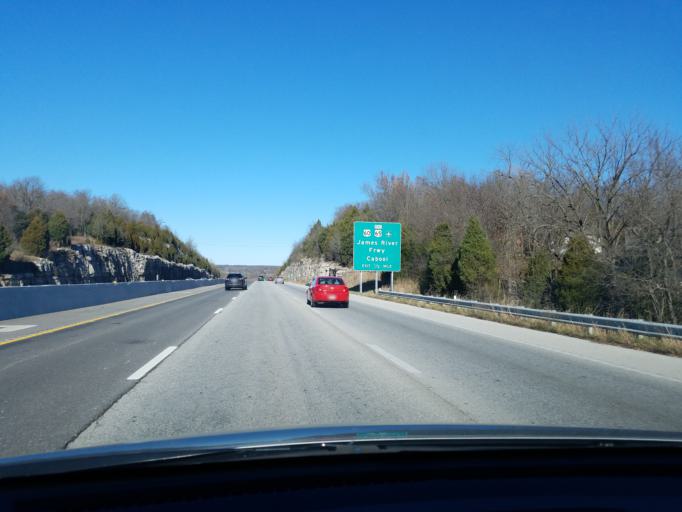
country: US
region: Missouri
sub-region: Christian County
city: Nixa
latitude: 37.1123
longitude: -93.2336
